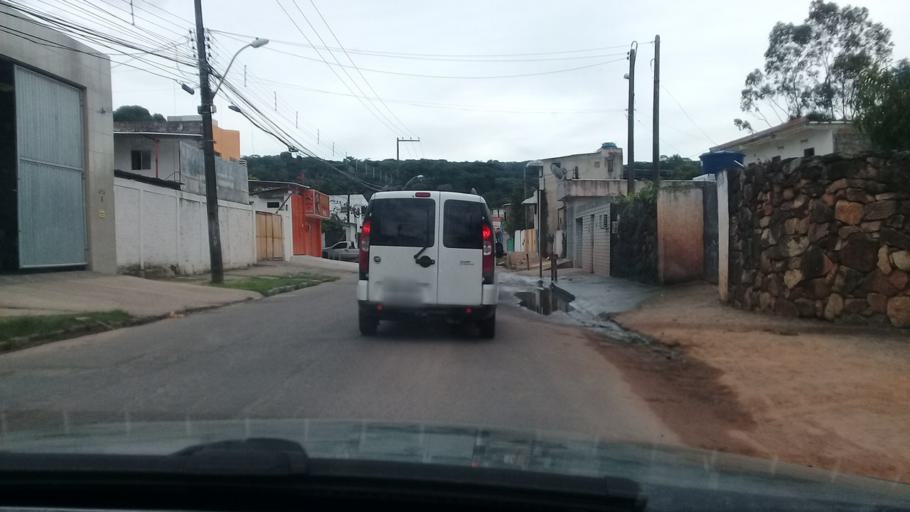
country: BR
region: Pernambuco
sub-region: Sao Lourenco Da Mata
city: Sao Lourenco da Mata
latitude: -8.0366
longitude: -34.9627
